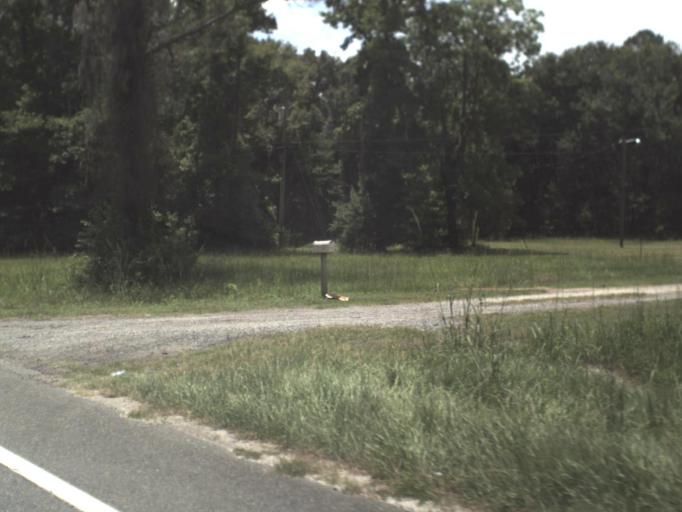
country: US
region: Florida
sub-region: Columbia County
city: Five Points
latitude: 30.2548
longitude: -82.6814
